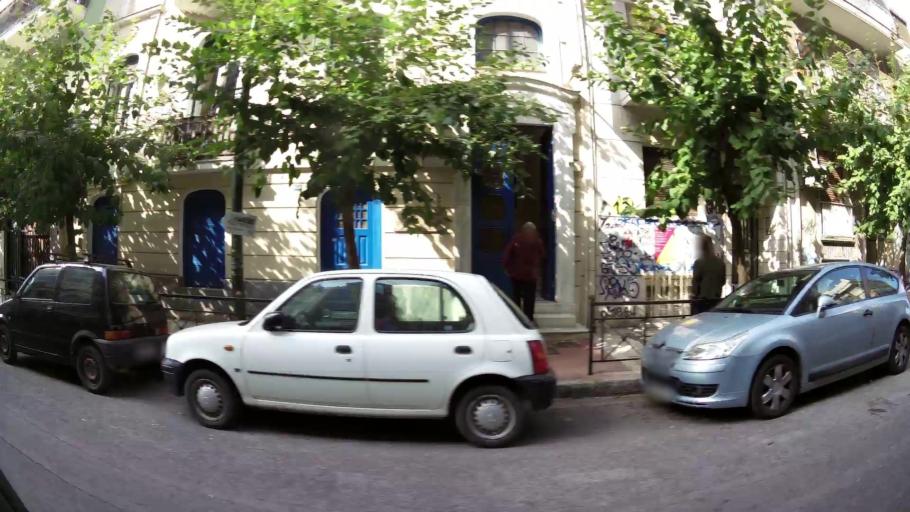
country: GR
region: Attica
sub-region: Nomarchia Athinas
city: Kipseli
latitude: 37.9923
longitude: 23.7287
